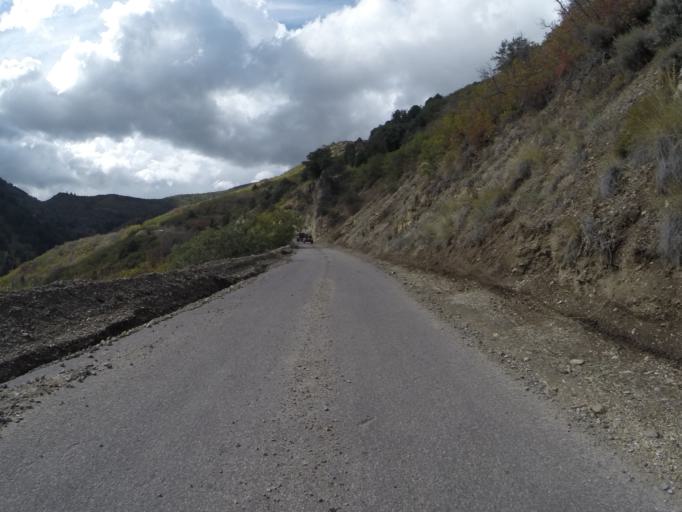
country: US
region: Utah
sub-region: Salt Lake County
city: Herriman
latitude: 40.4872
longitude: -112.1589
